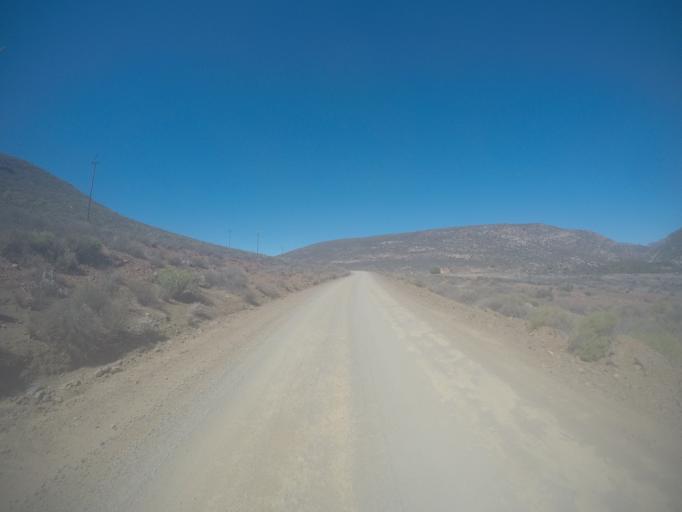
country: ZA
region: Western Cape
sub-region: West Coast District Municipality
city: Clanwilliam
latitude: -32.5208
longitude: 19.3509
